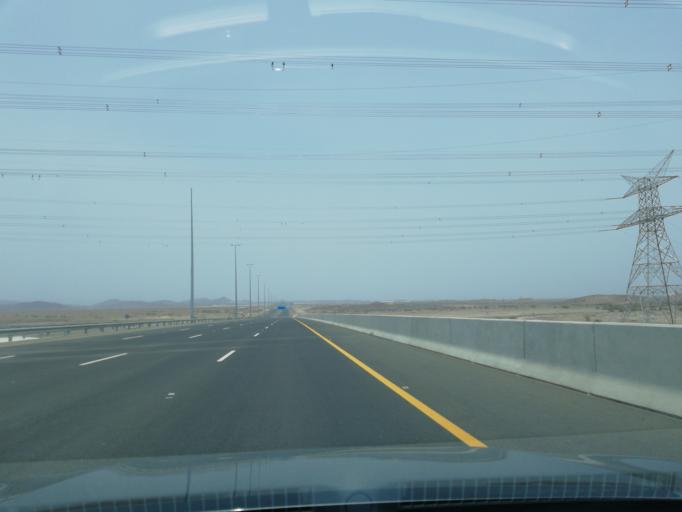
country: OM
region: Al Batinah
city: Al Liwa'
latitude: 24.4290
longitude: 56.5276
